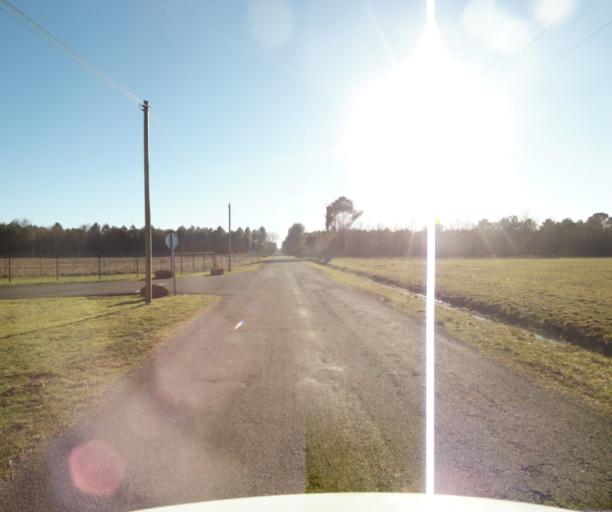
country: FR
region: Aquitaine
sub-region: Departement des Landes
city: Gabarret
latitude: 44.1243
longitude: -0.0961
